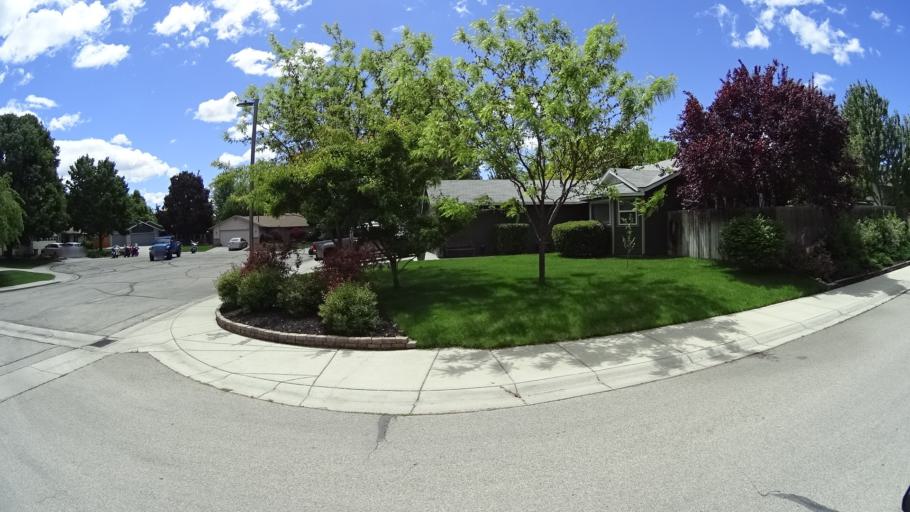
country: US
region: Idaho
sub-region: Ada County
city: Eagle
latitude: 43.6557
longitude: -116.3390
